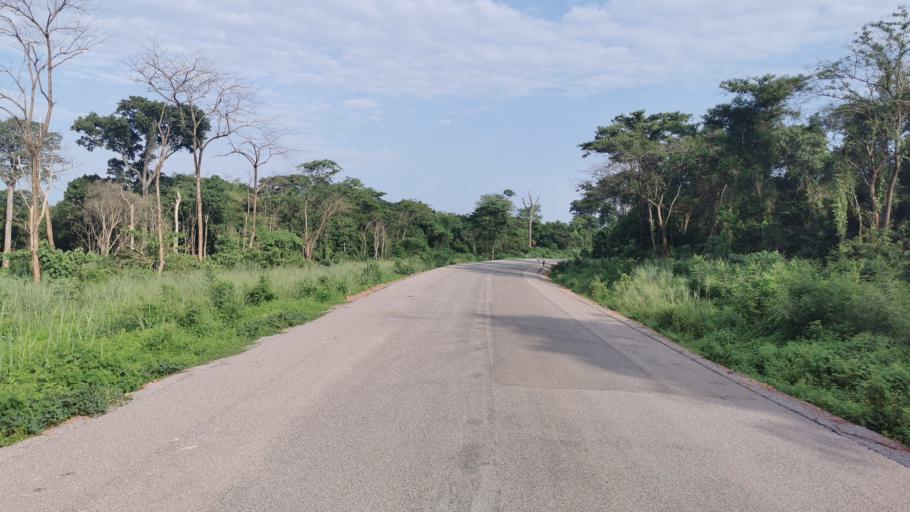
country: ET
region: Gambela
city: Gambela
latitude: 7.6695
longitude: 34.6767
